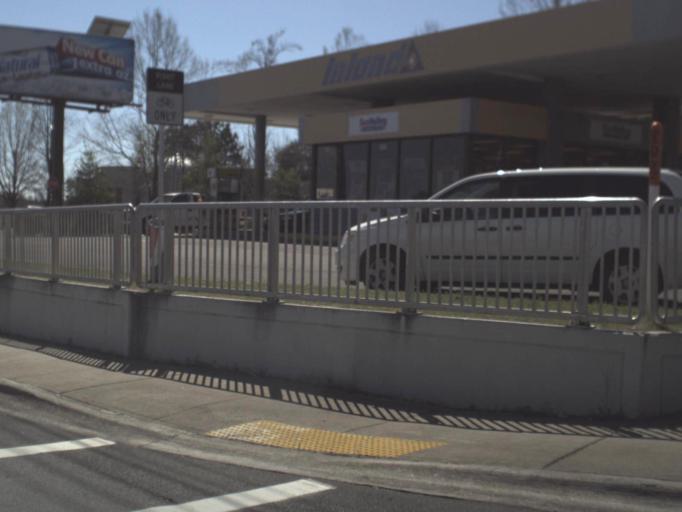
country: US
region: Florida
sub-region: Leon County
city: Tallahassee
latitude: 30.4632
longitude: -84.3613
